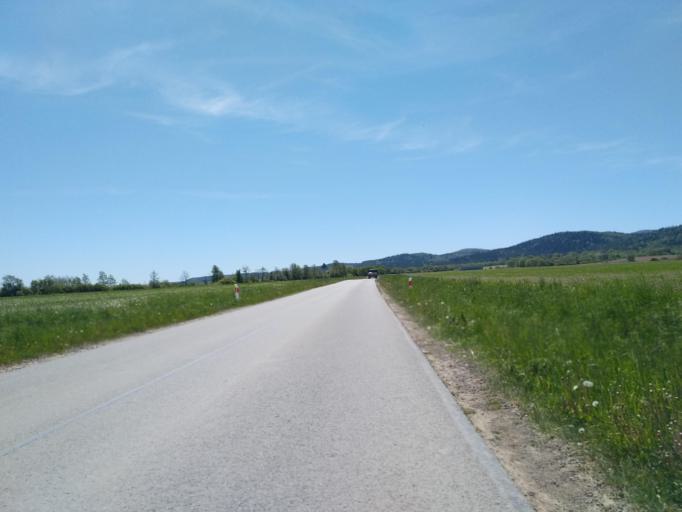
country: PL
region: Subcarpathian Voivodeship
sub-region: Powiat krosnienski
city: Sieniawa
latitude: 49.5357
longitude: 21.9721
